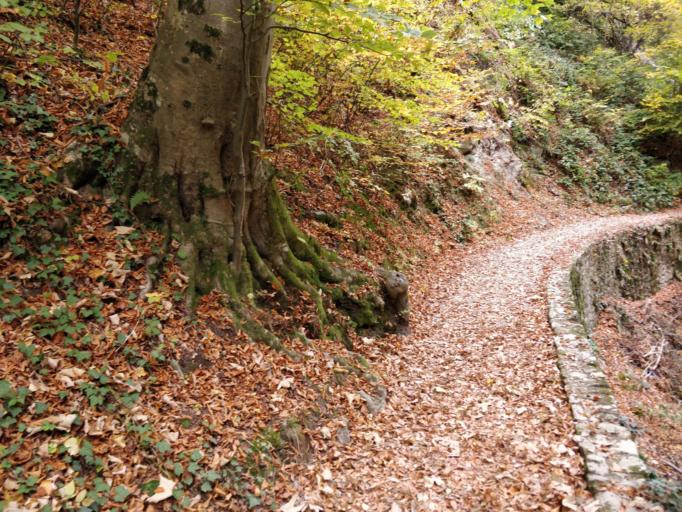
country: HR
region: Grad Zagreb
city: Zagreb
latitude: 45.8687
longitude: 15.9455
